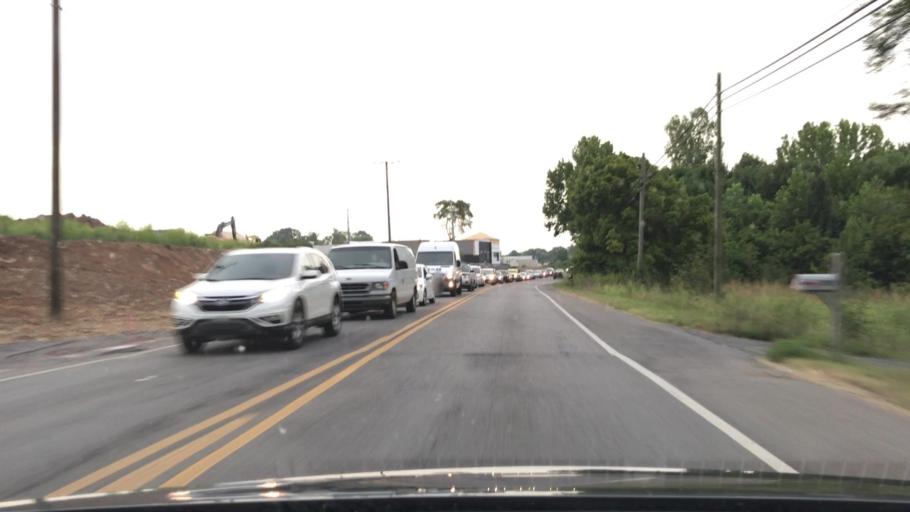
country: US
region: Tennessee
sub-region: Williamson County
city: Nolensville
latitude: 35.9904
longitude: -86.6828
